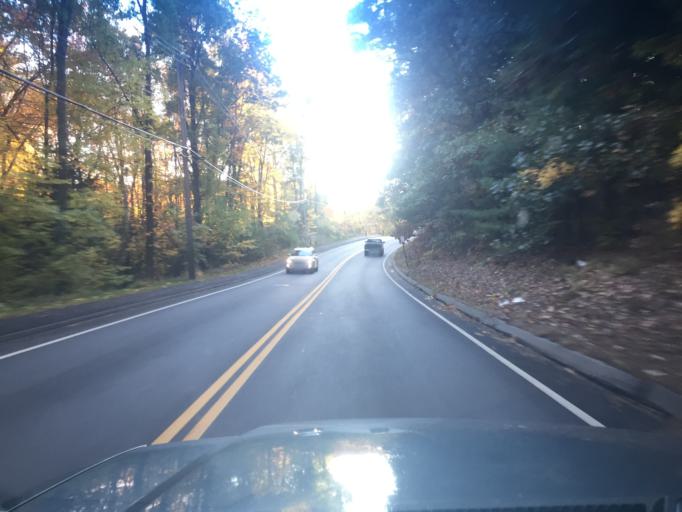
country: US
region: Massachusetts
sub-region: Middlesex County
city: Hudson
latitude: 42.3785
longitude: -71.5512
